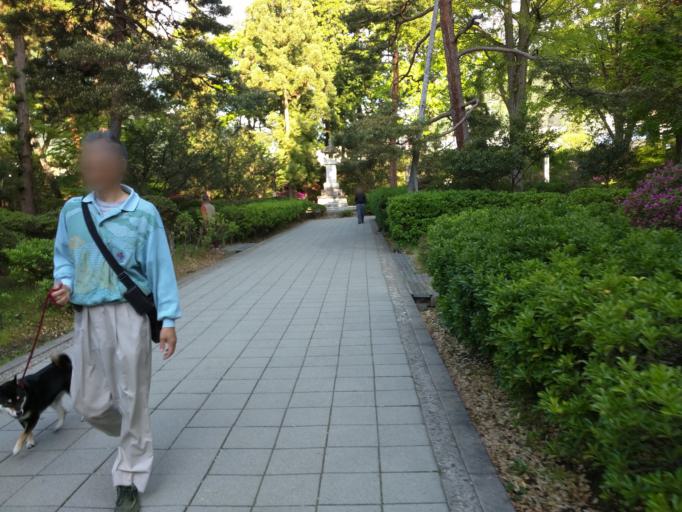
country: JP
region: Nagano
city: Nagano-shi
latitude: 36.6616
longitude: 138.1872
